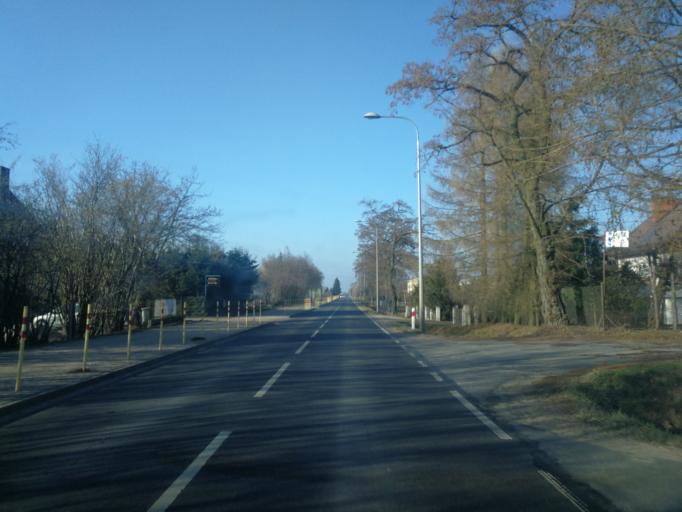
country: PL
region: Warmian-Masurian Voivodeship
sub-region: Powiat ilawski
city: Lubawa
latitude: 53.4785
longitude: 19.7647
